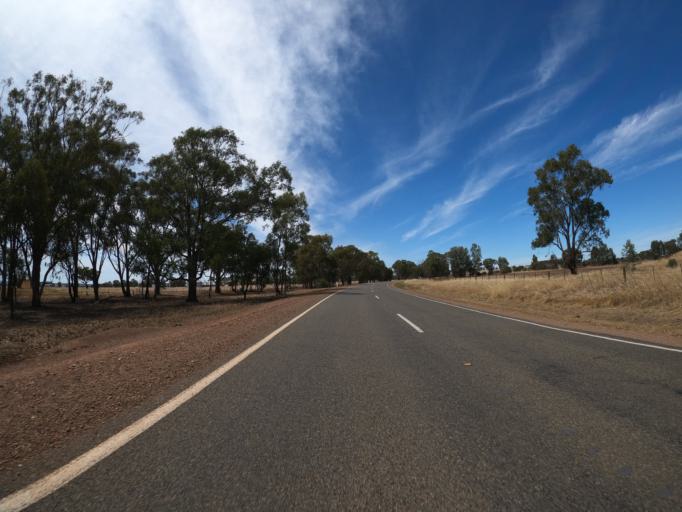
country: AU
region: Victoria
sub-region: Benalla
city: Benalla
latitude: -36.3066
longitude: 145.9580
